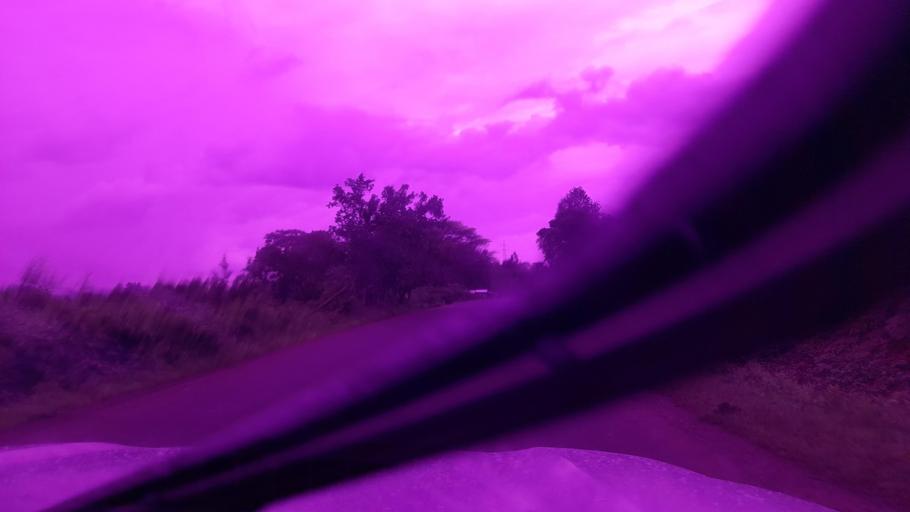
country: ET
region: Oromiya
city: Jima
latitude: 7.7082
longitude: 37.0298
